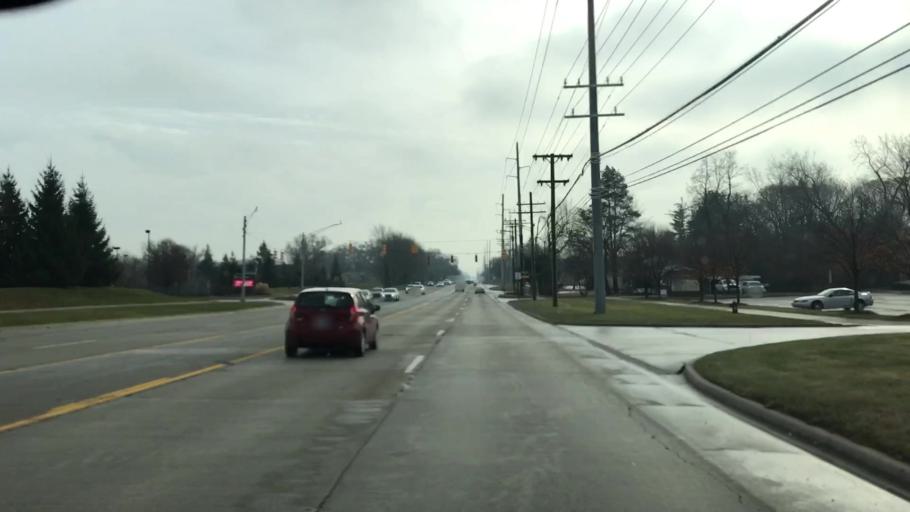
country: US
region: Michigan
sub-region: Oakland County
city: Troy
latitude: 42.6167
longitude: -83.1304
